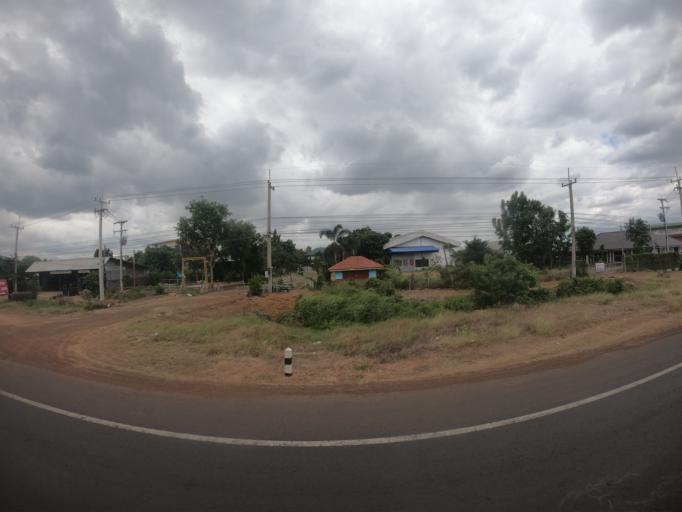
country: TH
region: Buriram
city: Nong Ki
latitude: 14.6808
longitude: 102.5519
